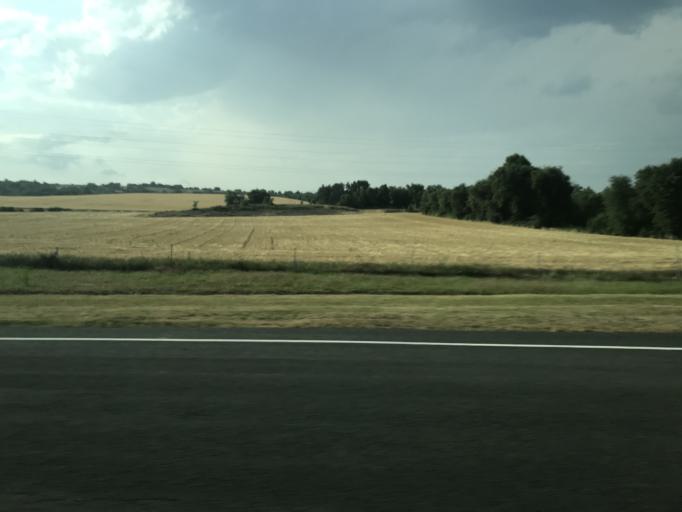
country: ES
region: Basque Country
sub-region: Provincia de Alava
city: Gasteiz / Vitoria
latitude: 42.9156
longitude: -2.6967
